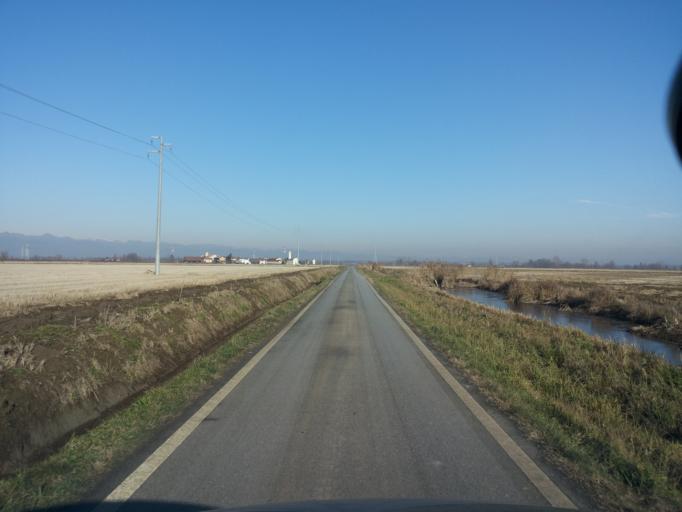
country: IT
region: Piedmont
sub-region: Provincia di Vercelli
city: Formigliana
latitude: 45.4291
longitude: 8.2566
